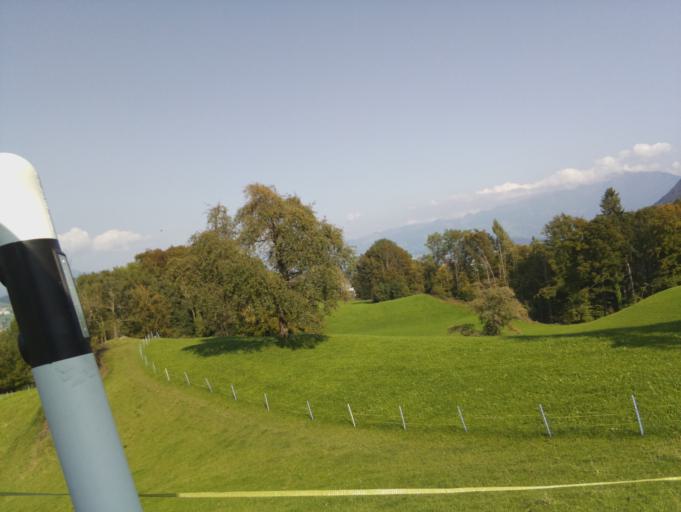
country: CH
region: Schwyz
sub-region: Bezirk March
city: Schubelbach
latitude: 47.1685
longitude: 8.8917
